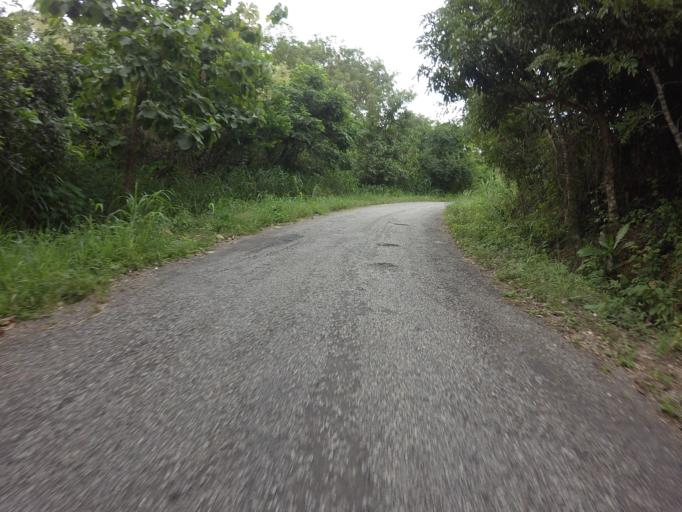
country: GH
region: Volta
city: Kpandu
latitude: 6.8830
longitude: 0.4436
